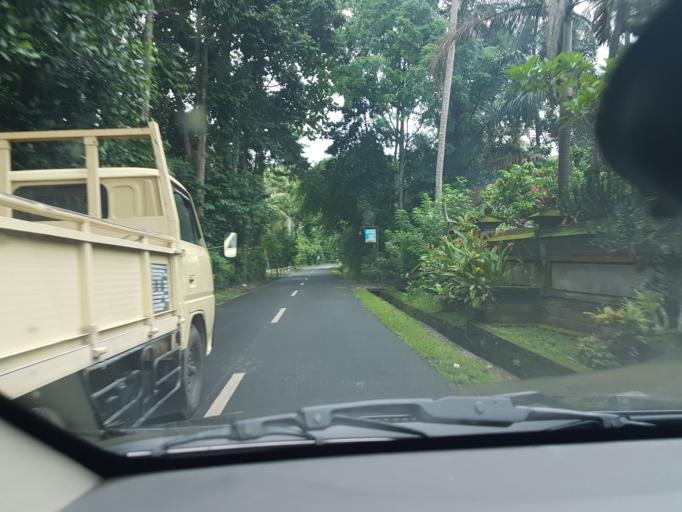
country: ID
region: Bali
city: Banjar Tebongkang
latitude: -8.5286
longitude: 115.2387
